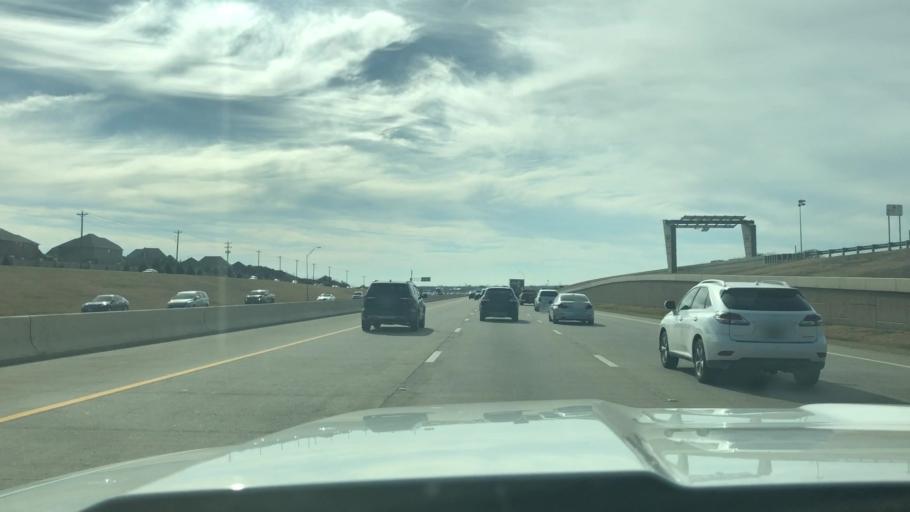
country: US
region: Texas
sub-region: Denton County
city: The Colony
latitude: 33.0346
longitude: -96.9257
